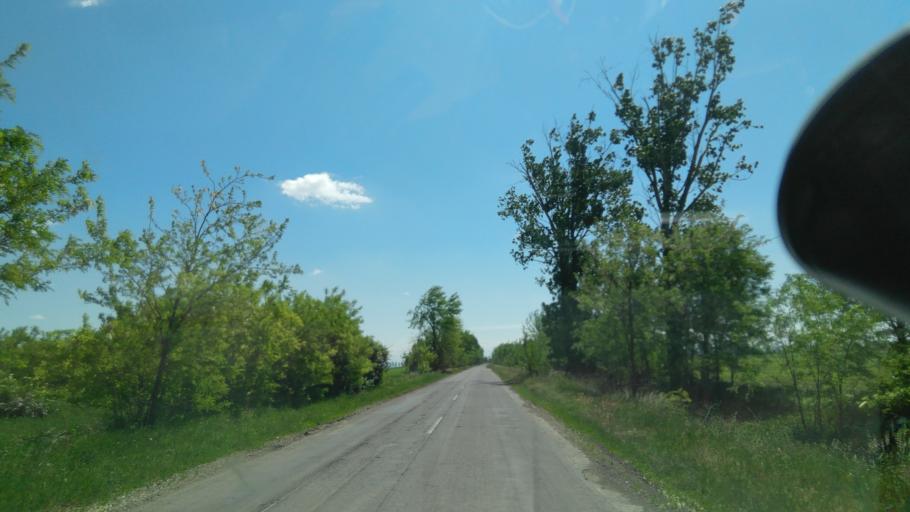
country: HU
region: Bekes
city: Kunagota
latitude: 46.4128
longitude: 21.0473
